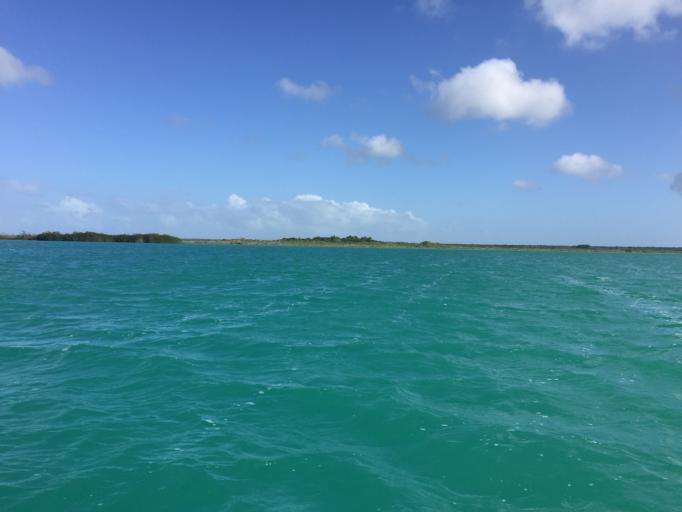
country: MX
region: Quintana Roo
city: Bacalar
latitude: 18.6351
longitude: -88.4099
